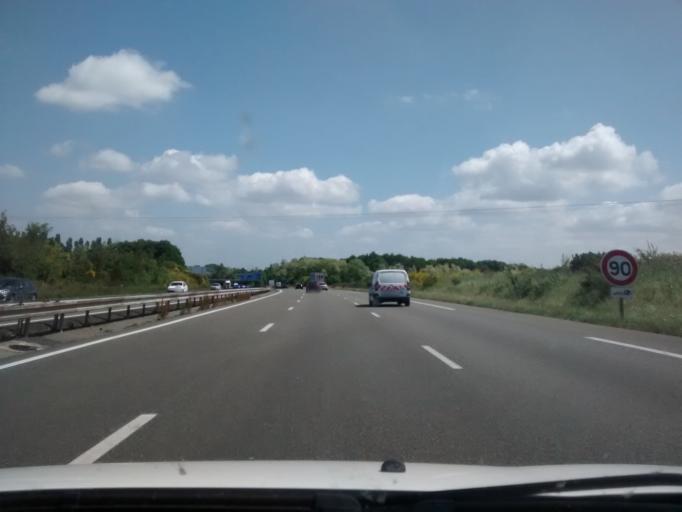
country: FR
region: Pays de la Loire
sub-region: Departement de la Sarthe
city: Sarge-les-le-Mans
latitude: 48.0506
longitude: 0.2681
